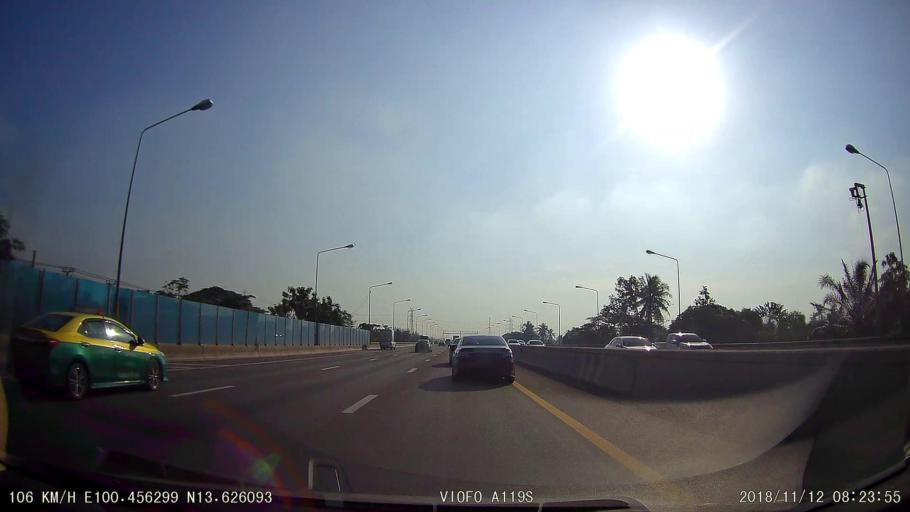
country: TH
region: Bangkok
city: Bang Khun Thian
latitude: 13.6254
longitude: 100.4567
